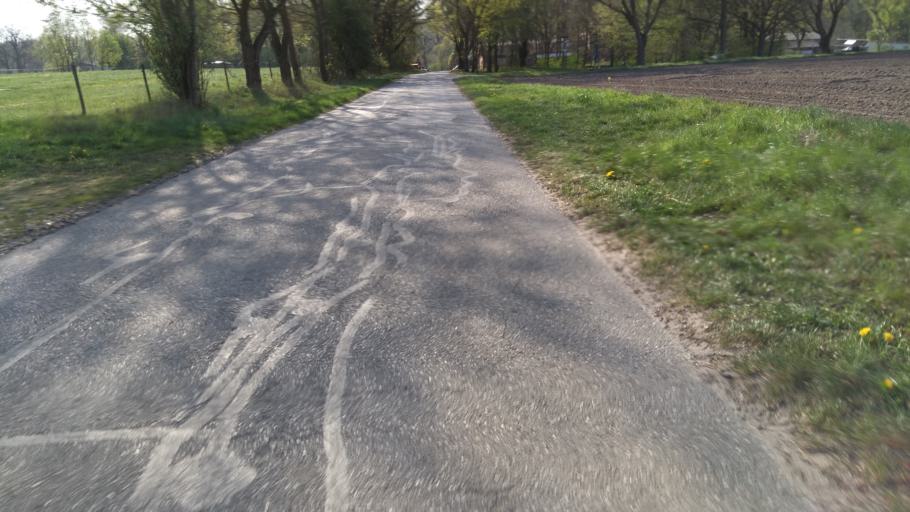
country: DE
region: Lower Saxony
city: Buxtehude
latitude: 53.4369
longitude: 9.6789
